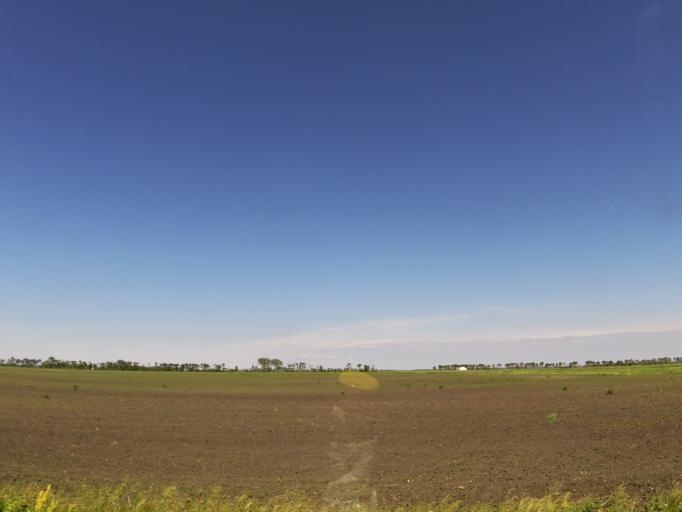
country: US
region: North Dakota
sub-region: Walsh County
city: Grafton
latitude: 48.3395
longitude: -97.2329
